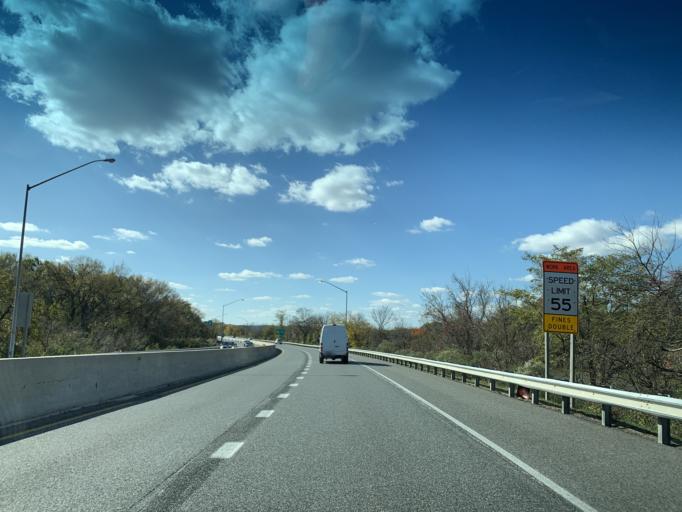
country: US
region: Maryland
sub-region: Anne Arundel County
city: Brooklyn Park
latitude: 39.2387
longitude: -76.6156
